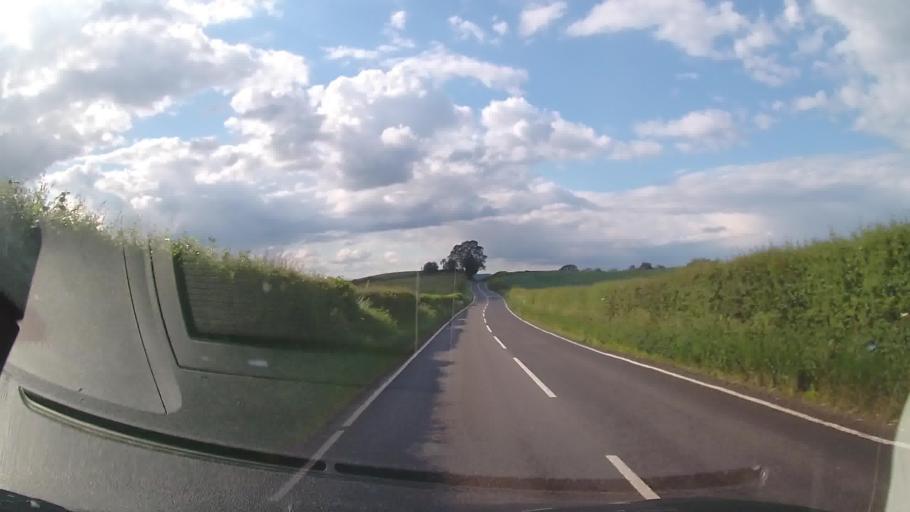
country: GB
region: England
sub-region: Shropshire
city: Kenley
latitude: 52.6582
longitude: -2.6174
